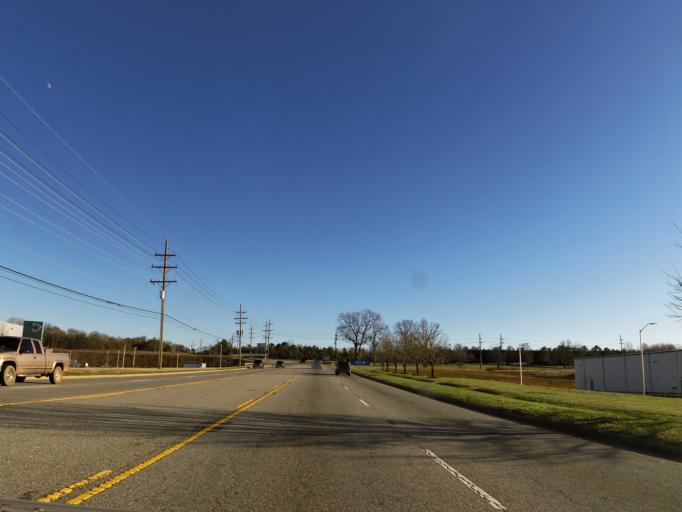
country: US
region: South Carolina
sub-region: Spartanburg County
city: Wellford
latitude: 34.8983
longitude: -82.0928
